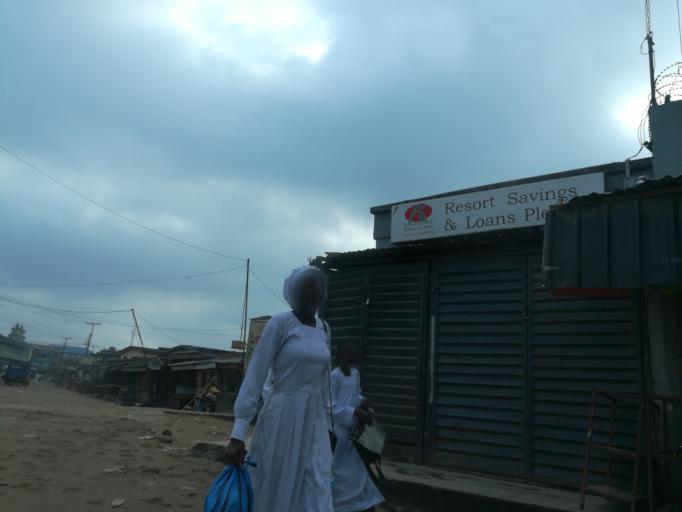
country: NG
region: Lagos
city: Agege
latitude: 6.6080
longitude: 3.3122
